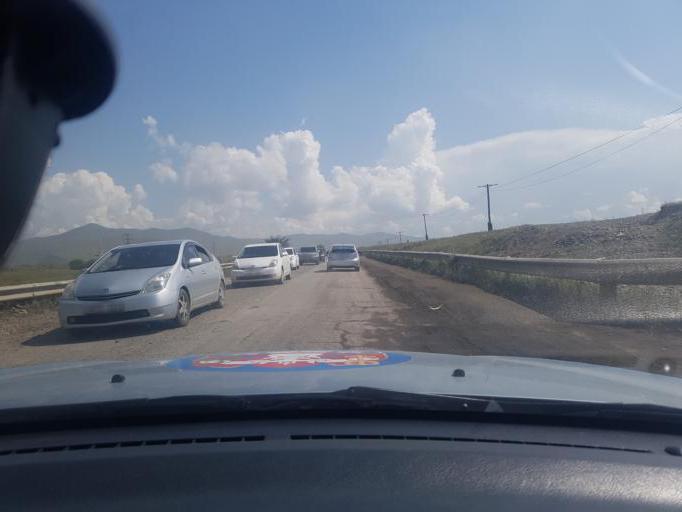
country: MN
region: Ulaanbaatar
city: Ulaanbaatar
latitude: 47.8962
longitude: 107.0493
